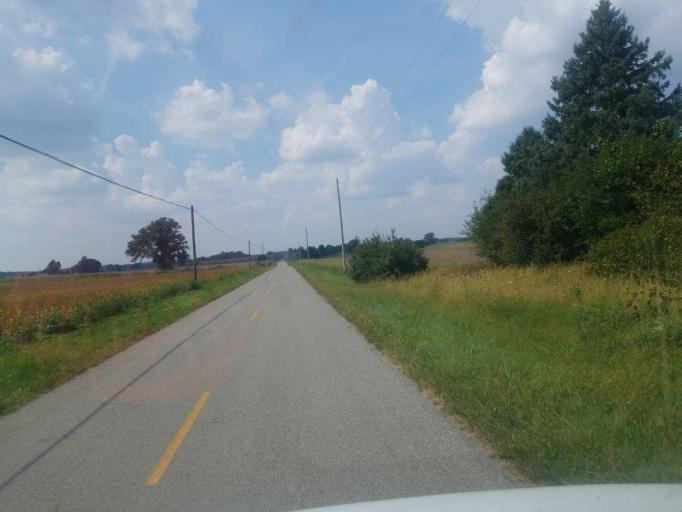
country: US
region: Ohio
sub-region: Logan County
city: Northwood
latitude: 40.6165
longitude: -83.7762
